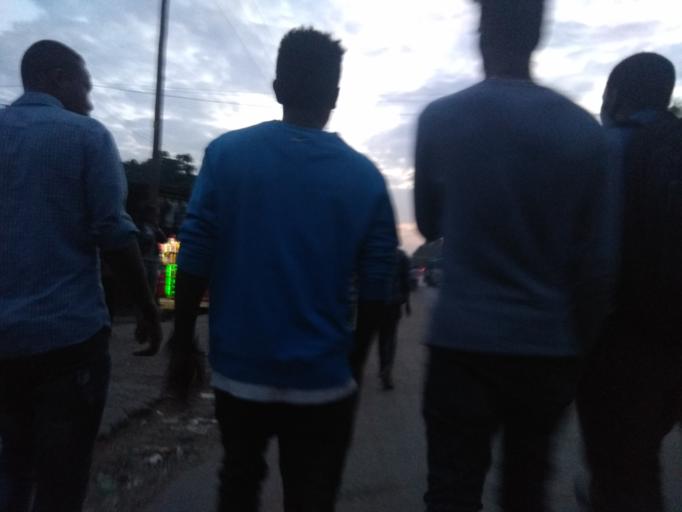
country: ET
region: Oromiya
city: Hagere Hiywet
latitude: 8.9820
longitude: 37.8553
